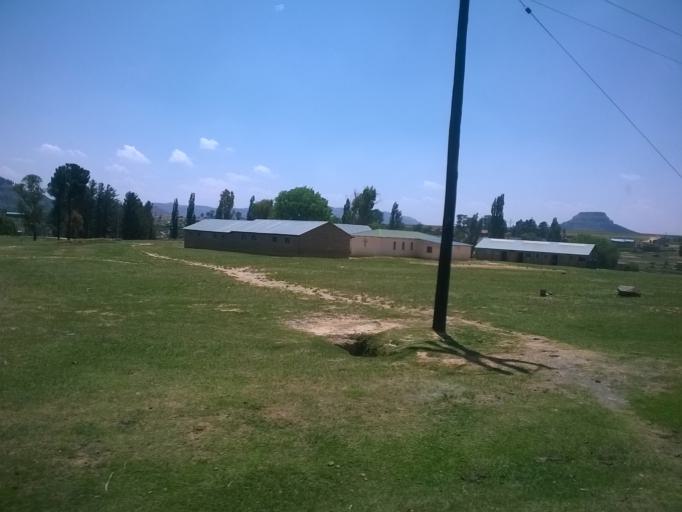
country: LS
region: Leribe
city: Maputsoe
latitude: -28.9731
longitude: 27.9746
